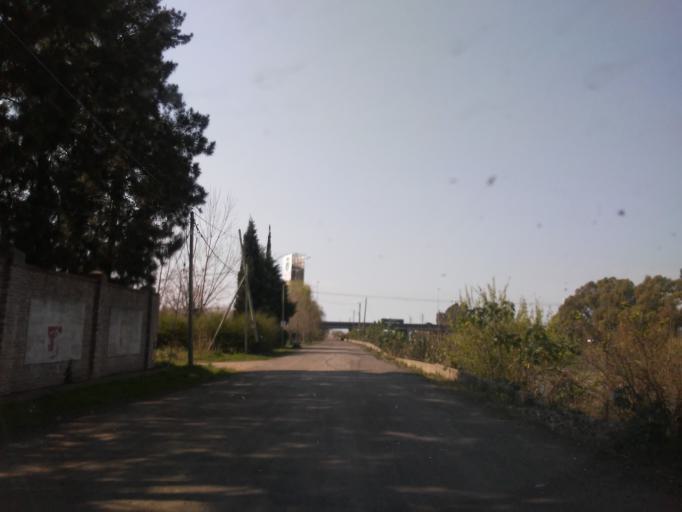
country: AR
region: Buenos Aires
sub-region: Partido de Avellaneda
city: Avellaneda
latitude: -34.6827
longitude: -58.3181
